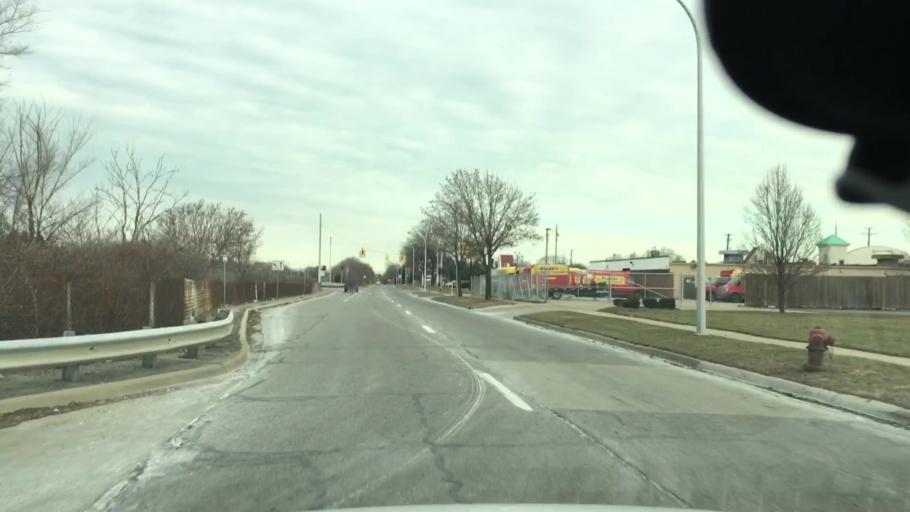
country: US
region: Michigan
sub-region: Oakland County
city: Madison Heights
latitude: 42.4908
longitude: -83.0687
